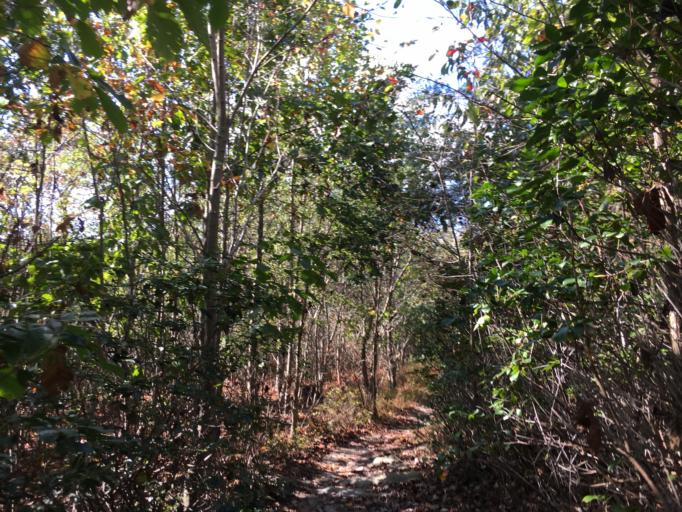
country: US
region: Pennsylvania
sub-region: York County
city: Yorklyn
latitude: 40.0089
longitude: -76.6522
